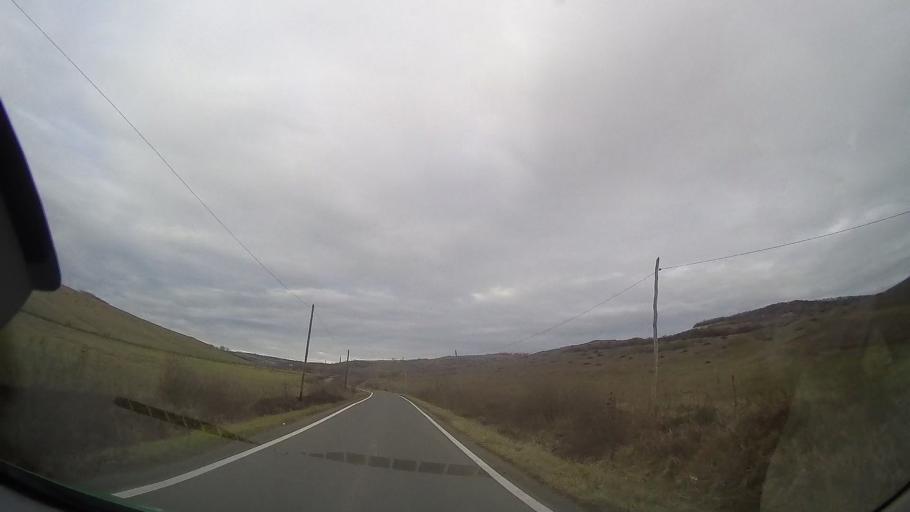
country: RO
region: Mures
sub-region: Comuna Cozma
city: Cozma
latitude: 46.7958
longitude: 24.5417
